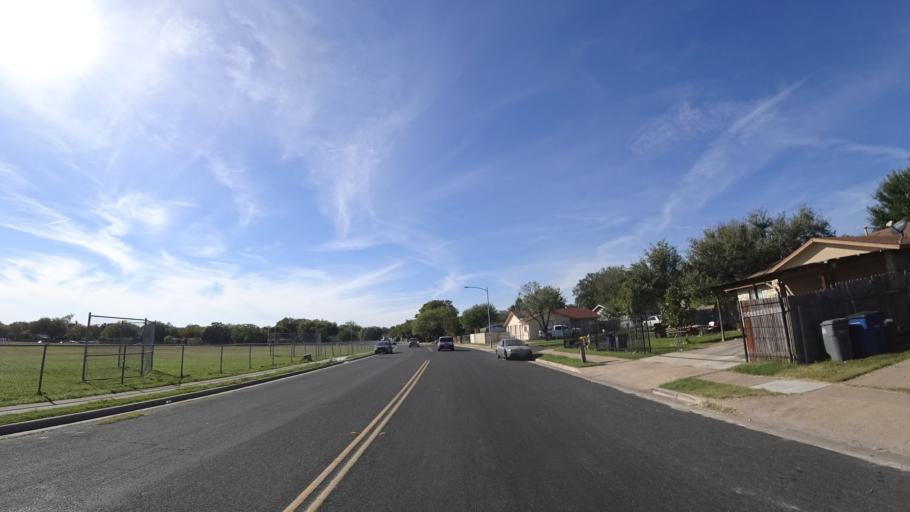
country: US
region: Texas
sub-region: Travis County
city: Onion Creek
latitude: 30.1904
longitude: -97.7430
